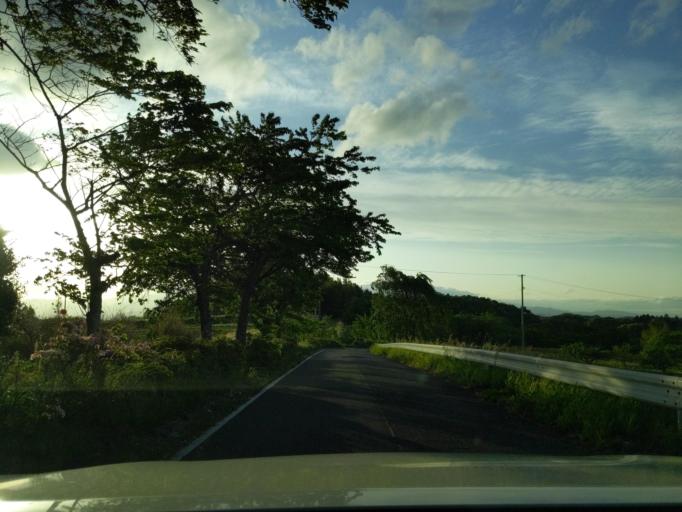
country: JP
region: Fukushima
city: Miharu
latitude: 37.4163
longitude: 140.4707
